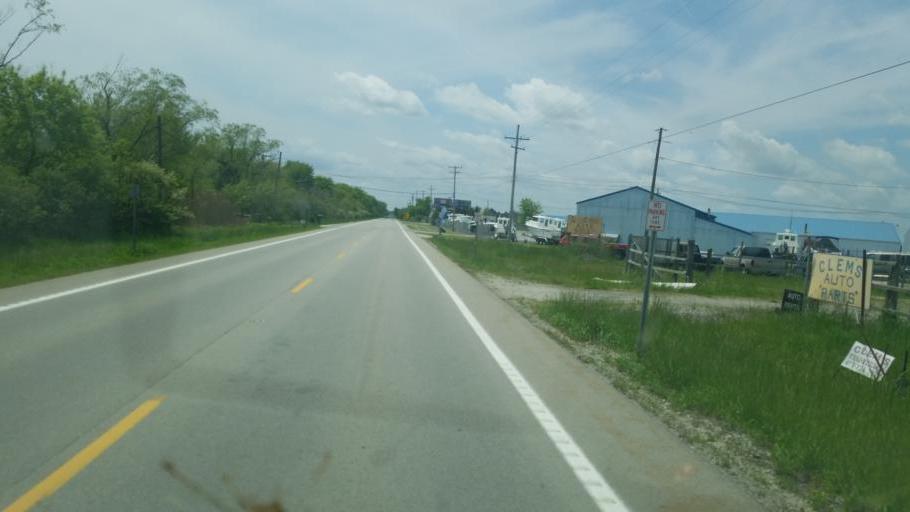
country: US
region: Ohio
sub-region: Ottawa County
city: Port Clinton
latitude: 41.4813
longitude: -83.0130
